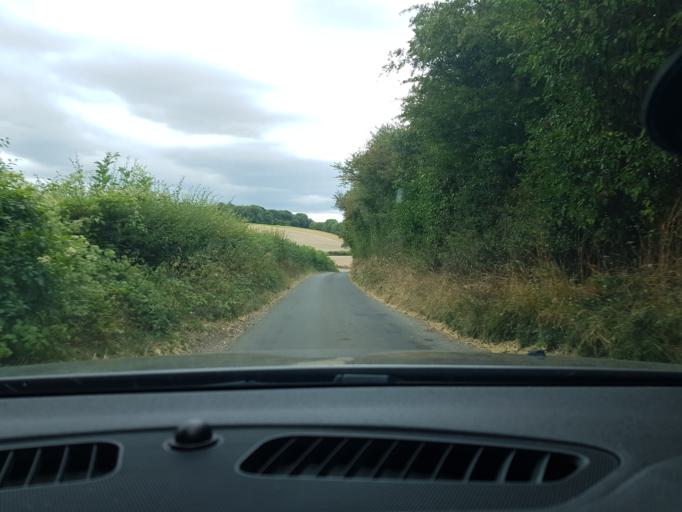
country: GB
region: England
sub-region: West Berkshire
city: Lambourn
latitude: 51.4842
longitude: -1.4997
